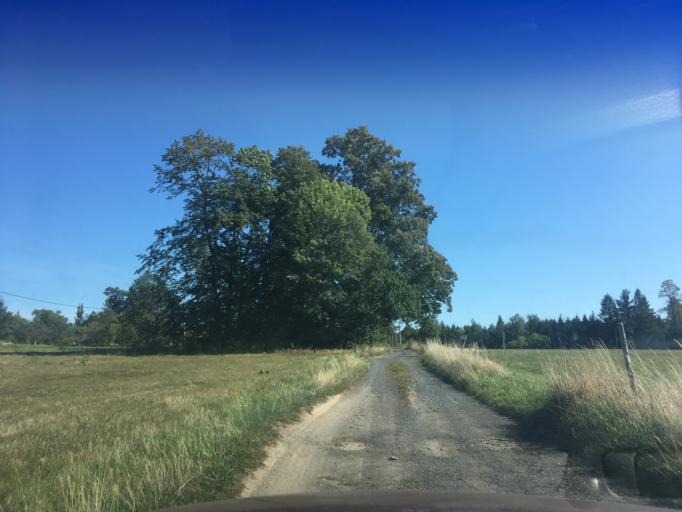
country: PL
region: Lower Silesian Voivodeship
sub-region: Powiat lubanski
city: Lesna
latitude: 50.9775
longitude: 15.3024
